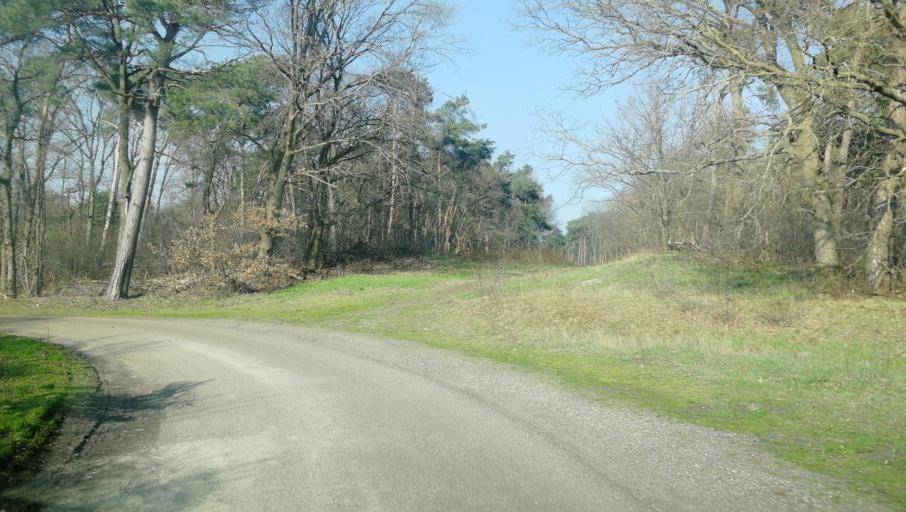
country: NL
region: Limburg
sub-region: Gemeente Venlo
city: Venlo
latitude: 51.3981
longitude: 6.1785
